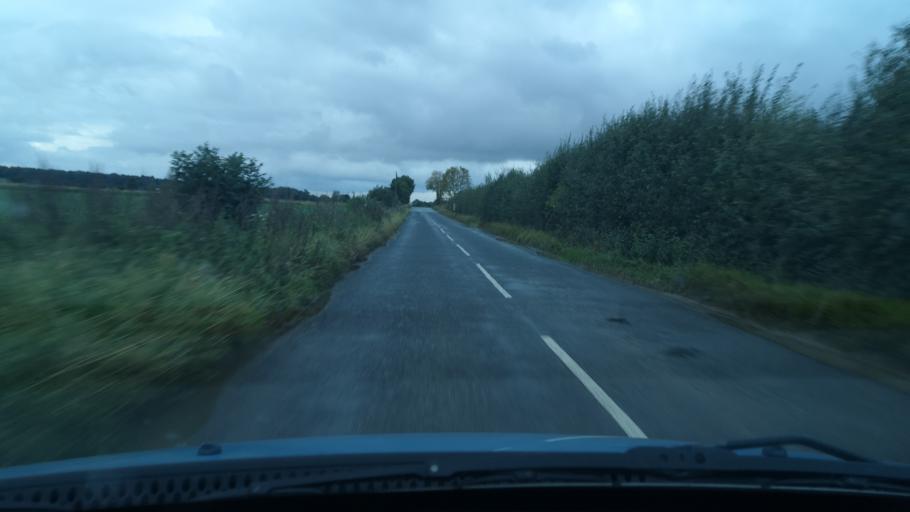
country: GB
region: England
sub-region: City and Borough of Wakefield
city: Darrington
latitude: 53.6462
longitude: -1.2466
